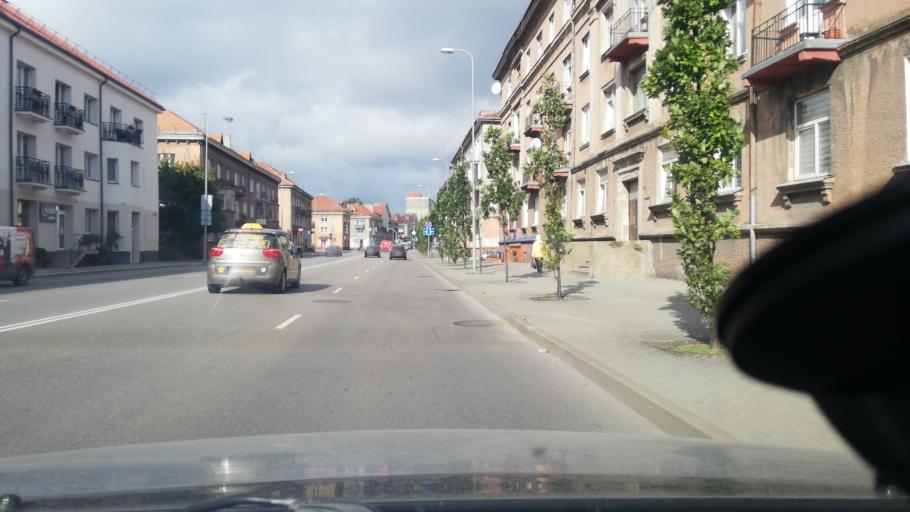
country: LT
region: Klaipedos apskritis
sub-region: Klaipeda
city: Klaipeda
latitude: 55.6766
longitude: 21.1539
